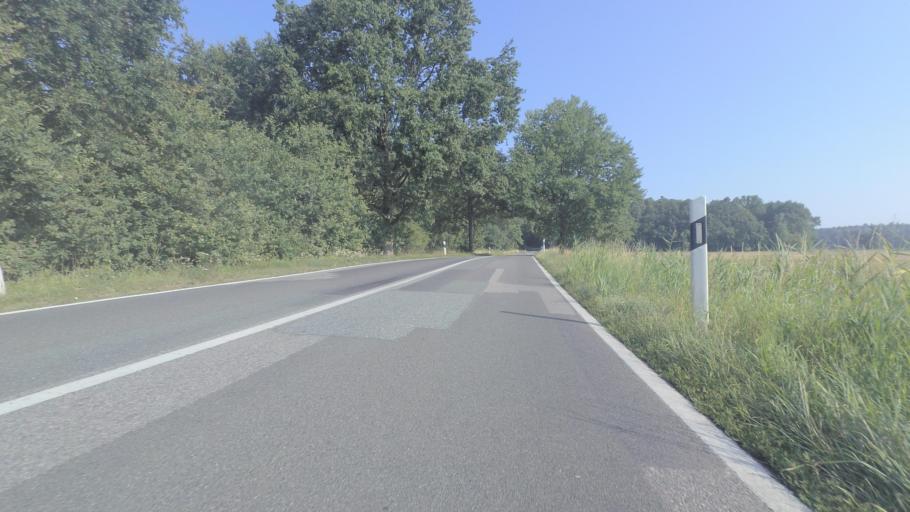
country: DE
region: Mecklenburg-Vorpommern
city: Malchow
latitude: 53.4499
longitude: 12.4310
